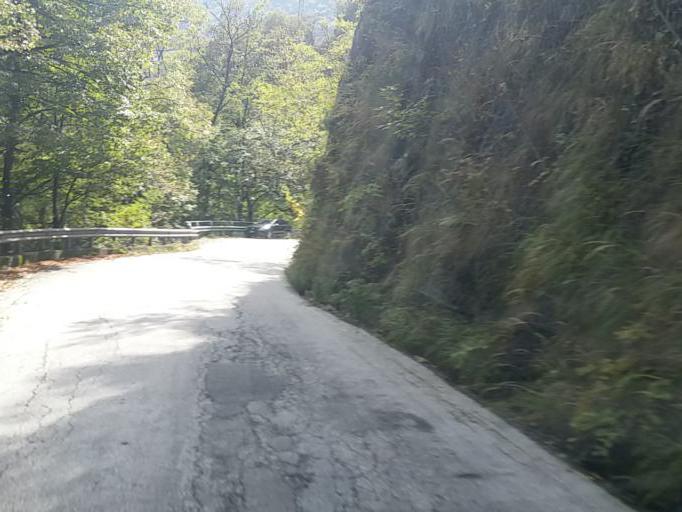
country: IT
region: Piedmont
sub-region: Provincia Verbano-Cusio-Ossola
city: Trarego
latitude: 46.0639
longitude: 8.6651
